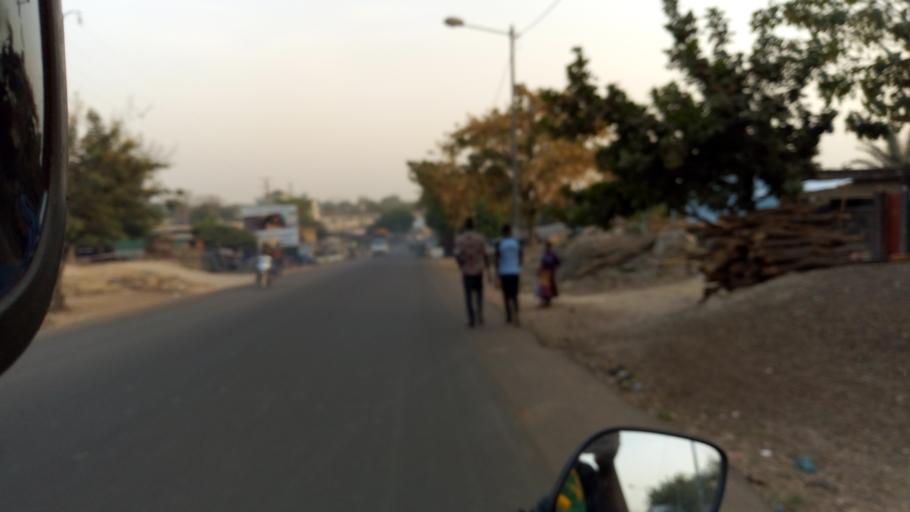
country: TG
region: Kara
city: Kara
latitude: 9.5516
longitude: 1.1967
